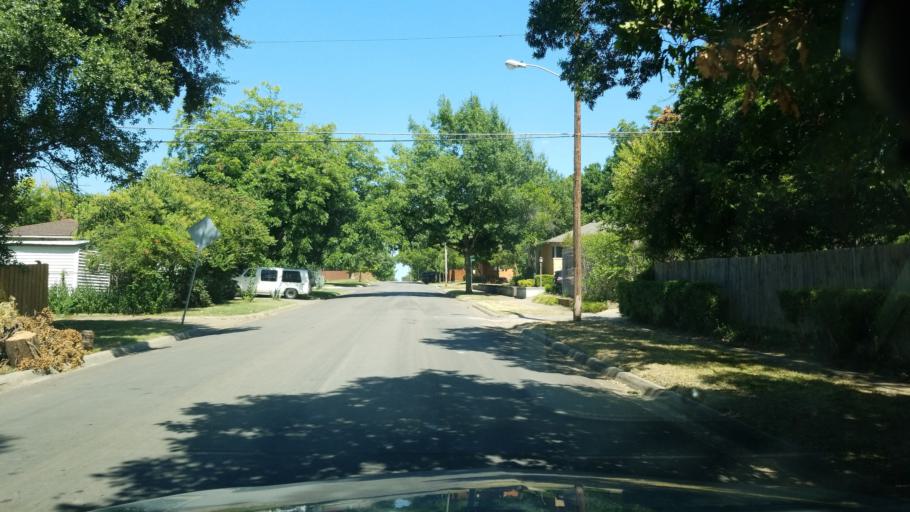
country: US
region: Texas
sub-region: Dallas County
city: Cockrell Hill
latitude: 32.7316
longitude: -96.8552
